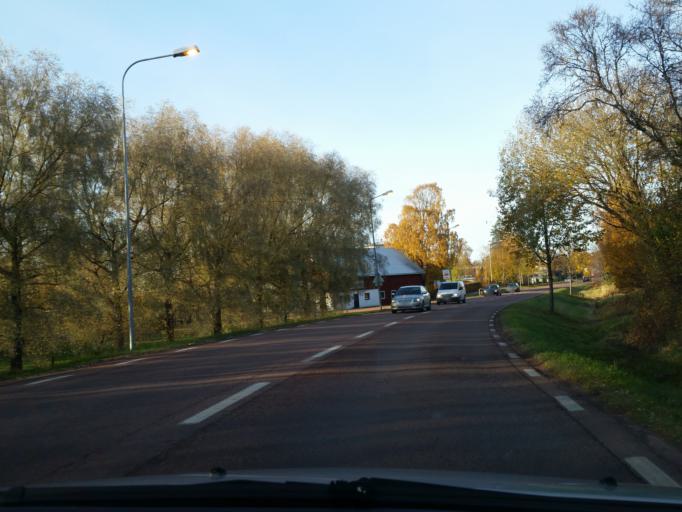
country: AX
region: Mariehamns stad
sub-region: Mariehamn
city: Mariehamn
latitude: 60.1078
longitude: 19.9311
